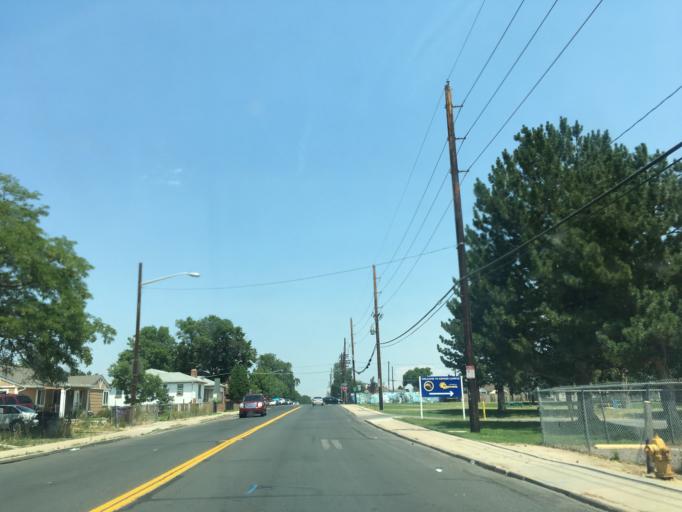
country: US
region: Colorado
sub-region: Jefferson County
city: Lakewood
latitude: 39.6993
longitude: -105.0298
